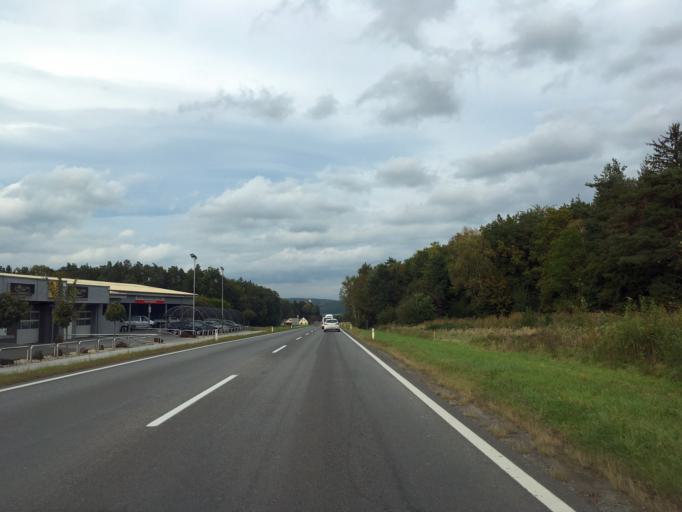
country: AT
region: Styria
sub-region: Politischer Bezirk Hartberg-Fuerstenfeld
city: Hartberg
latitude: 47.3164
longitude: 15.9834
